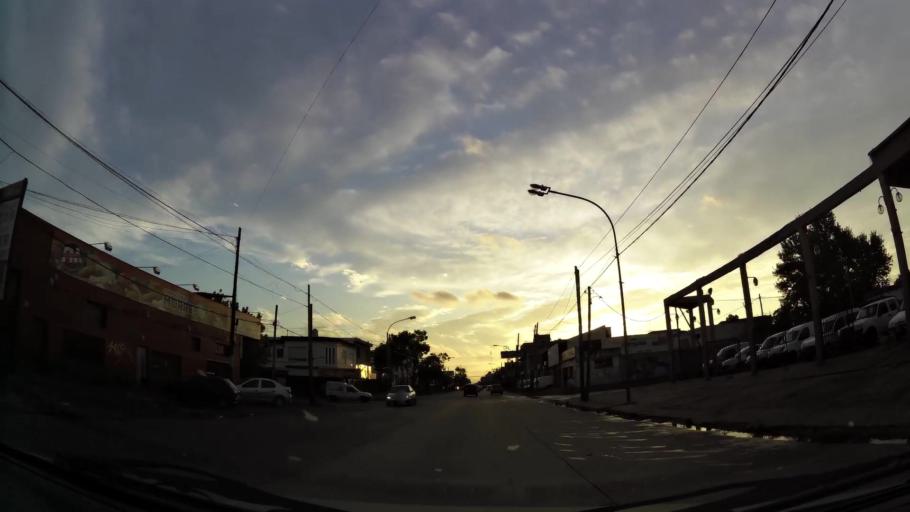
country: AR
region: Buenos Aires
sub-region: Partido de Lomas de Zamora
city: Lomas de Zamora
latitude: -34.7675
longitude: -58.3737
